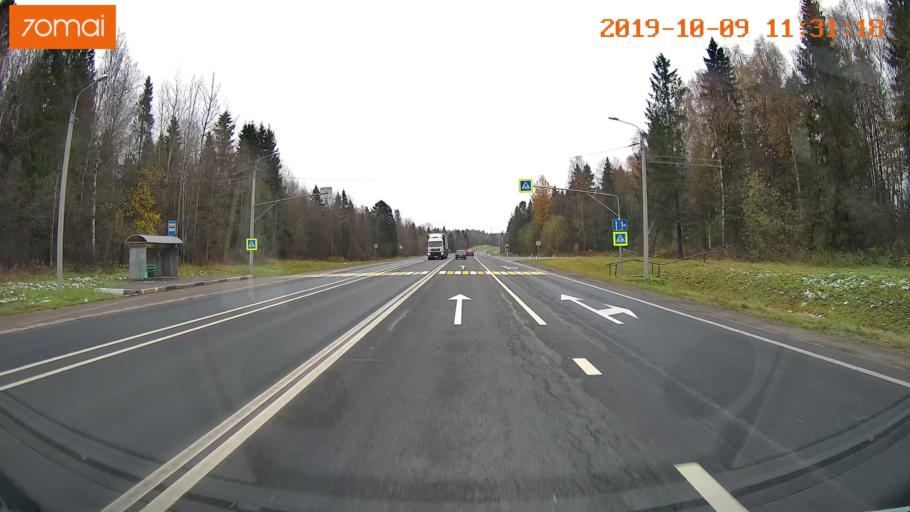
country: RU
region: Vologda
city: Gryazovets
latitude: 59.0468
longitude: 40.0930
